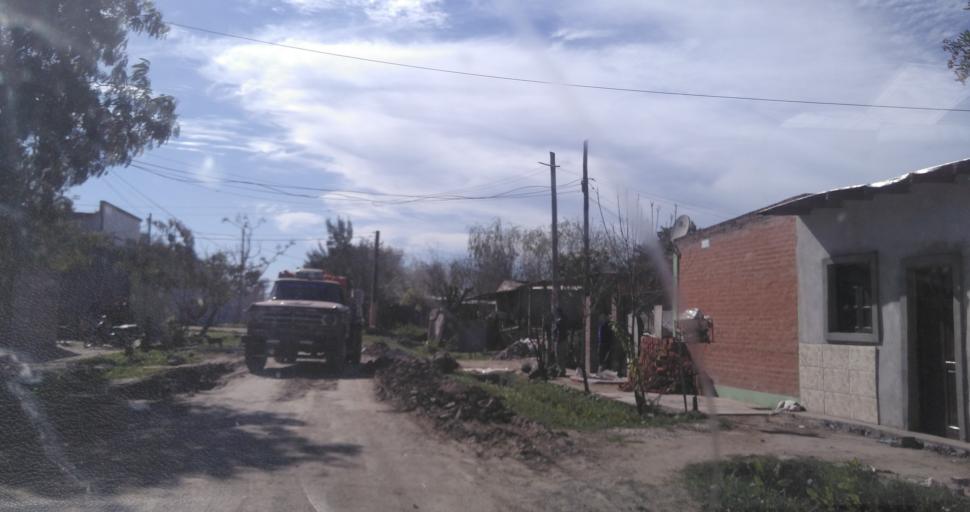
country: AR
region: Chaco
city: Fontana
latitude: -27.4356
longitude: -59.0240
